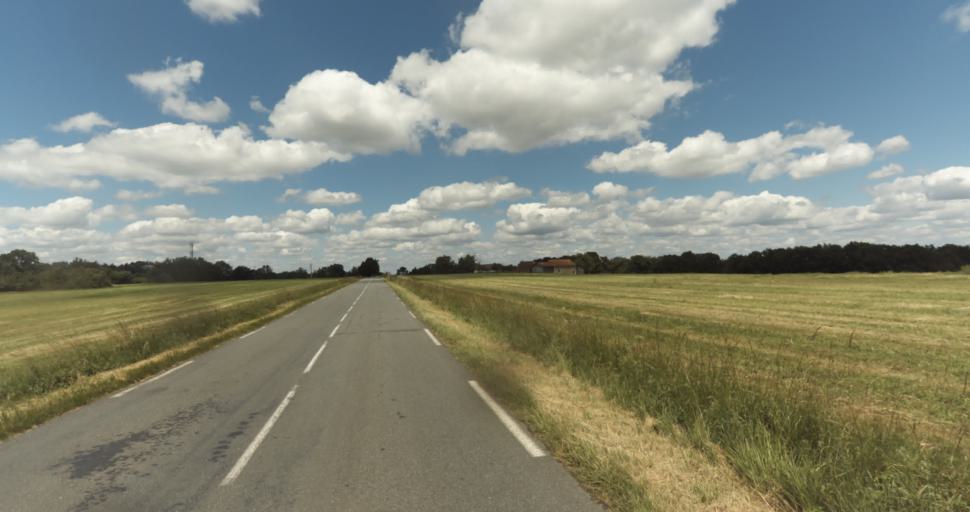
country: FR
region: Aquitaine
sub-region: Departement de la Dordogne
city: Beaumont-du-Perigord
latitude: 44.7454
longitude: 0.7801
